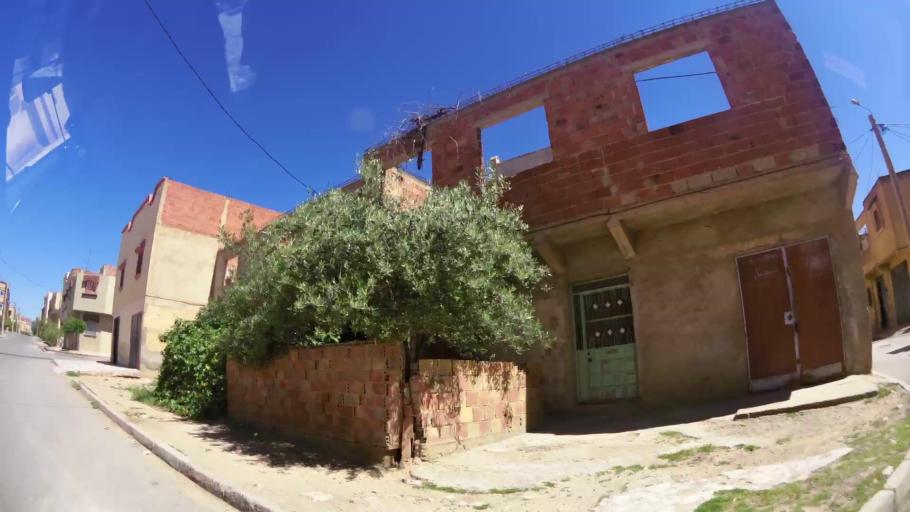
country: MA
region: Oriental
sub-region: Oujda-Angad
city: Oujda
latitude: 34.6623
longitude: -1.8787
